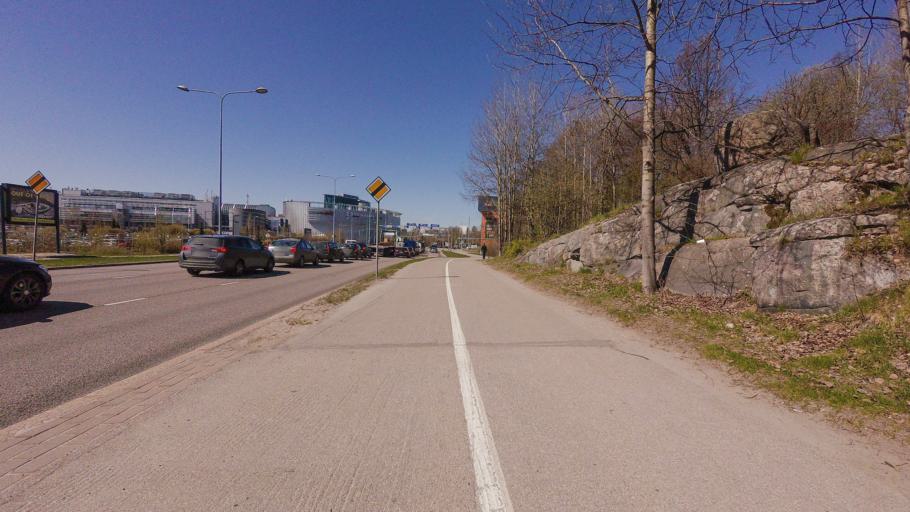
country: FI
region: Uusimaa
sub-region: Helsinki
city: Vantaa
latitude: 60.2113
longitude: 25.0893
